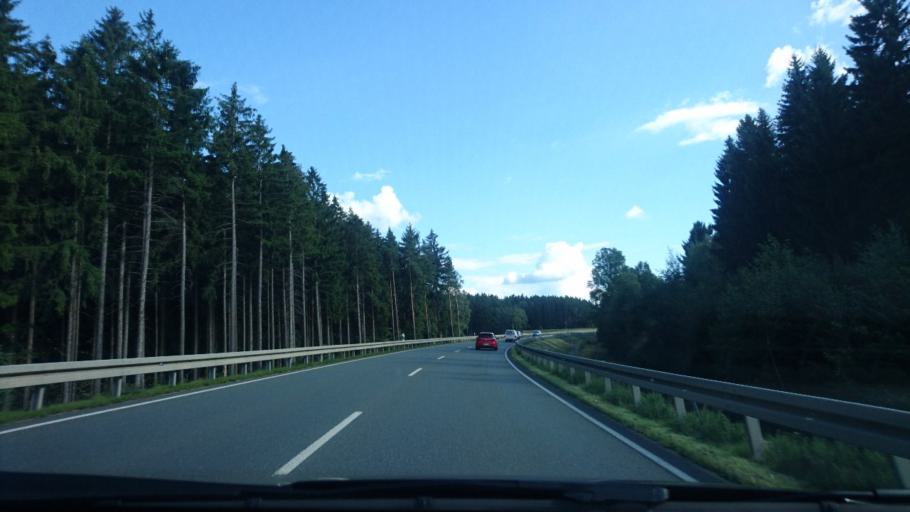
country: DE
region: Saxony
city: Lengenfeld
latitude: 50.5360
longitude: 12.3724
